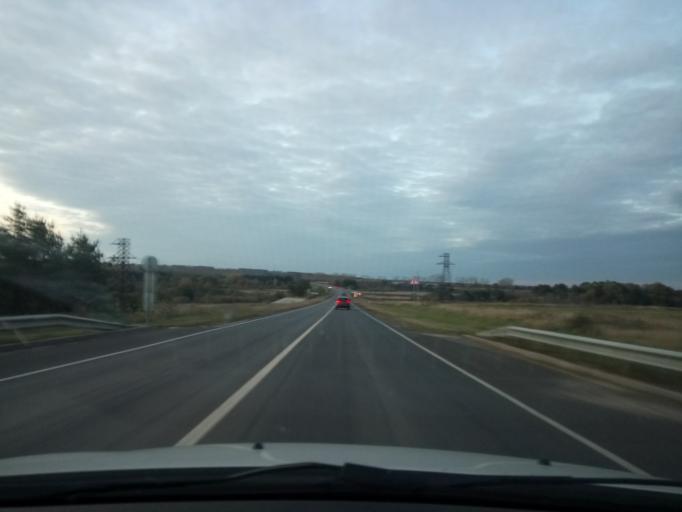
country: RU
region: Nizjnij Novgorod
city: Bol'shoye Murashkino
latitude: 55.8769
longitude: 44.7479
